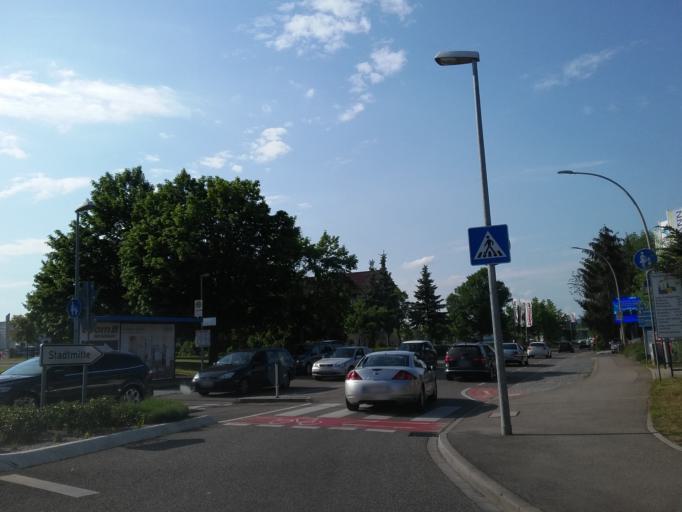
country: DE
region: Baden-Wuerttemberg
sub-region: Regierungsbezirk Stuttgart
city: Backnang
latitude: 48.9332
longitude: 9.4467
